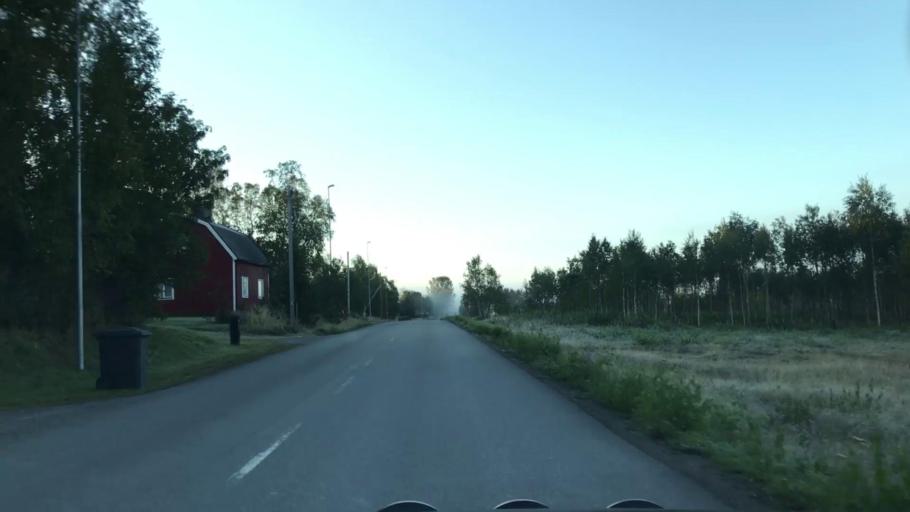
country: SE
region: Norrbotten
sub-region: Gallivare Kommun
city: Malmberget
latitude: 67.6502
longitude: 21.0440
